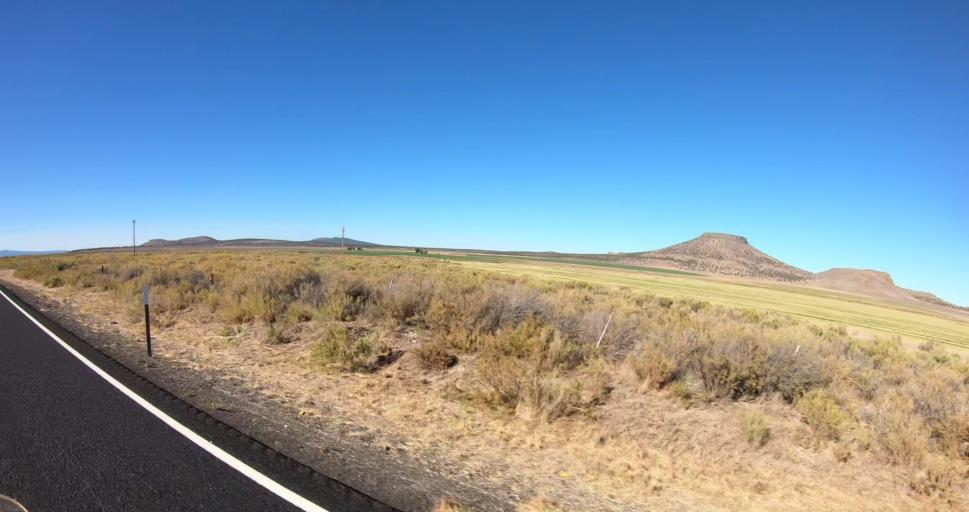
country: US
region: Oregon
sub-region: Deschutes County
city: La Pine
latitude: 43.1295
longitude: -120.8990
